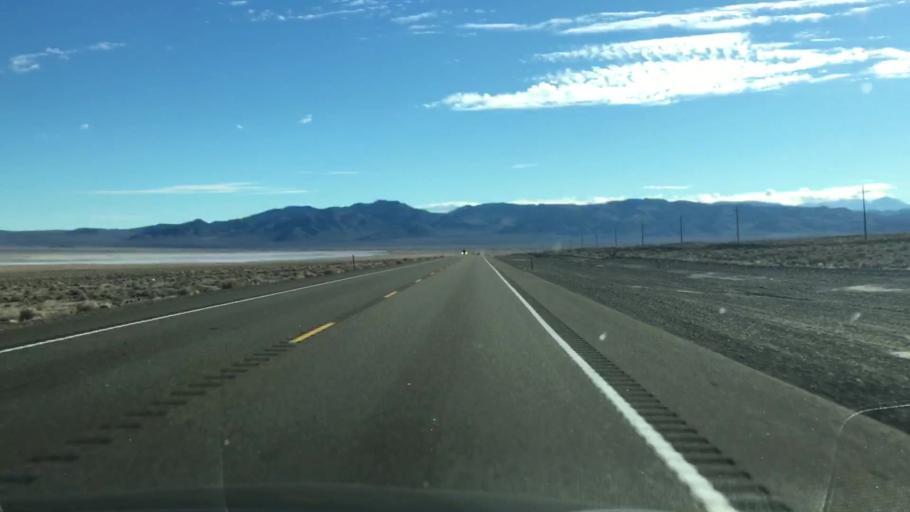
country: US
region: Nevada
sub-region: Mineral County
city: Hawthorne
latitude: 38.3197
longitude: -118.1029
